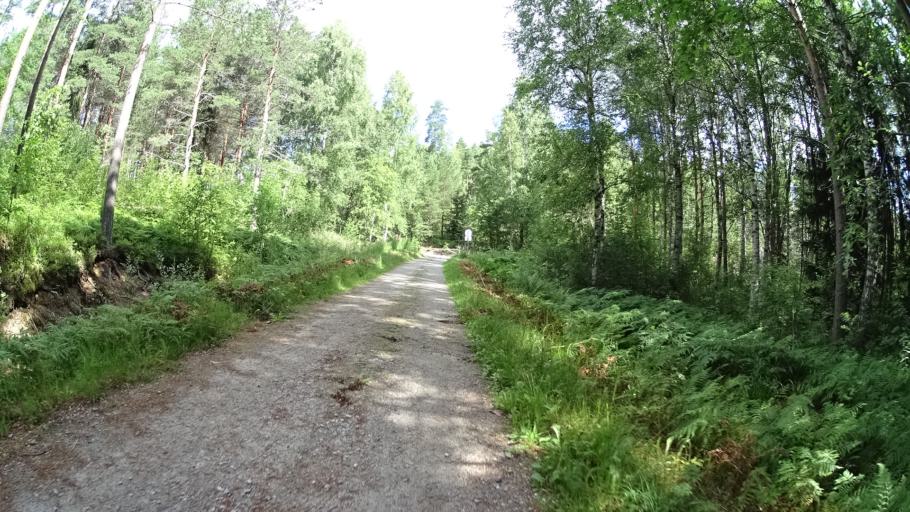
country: FI
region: Uusimaa
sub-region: Helsinki
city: Espoo
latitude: 60.3569
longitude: 24.6669
